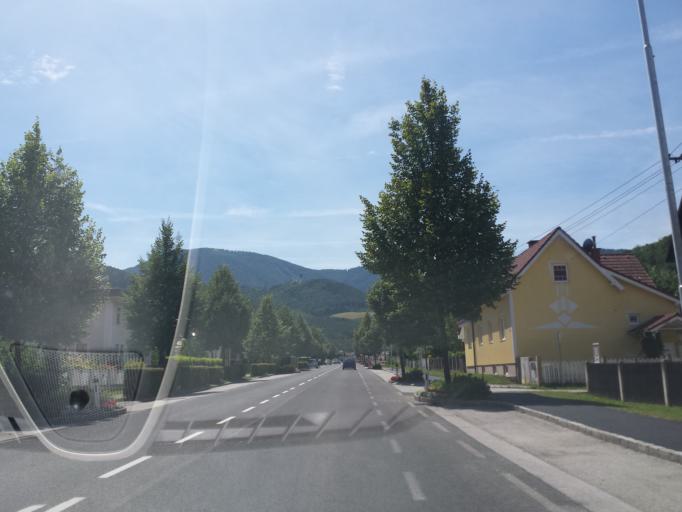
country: AT
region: Lower Austria
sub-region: Politischer Bezirk Neunkirchen
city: Gloggnitz
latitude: 47.6695
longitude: 15.9302
